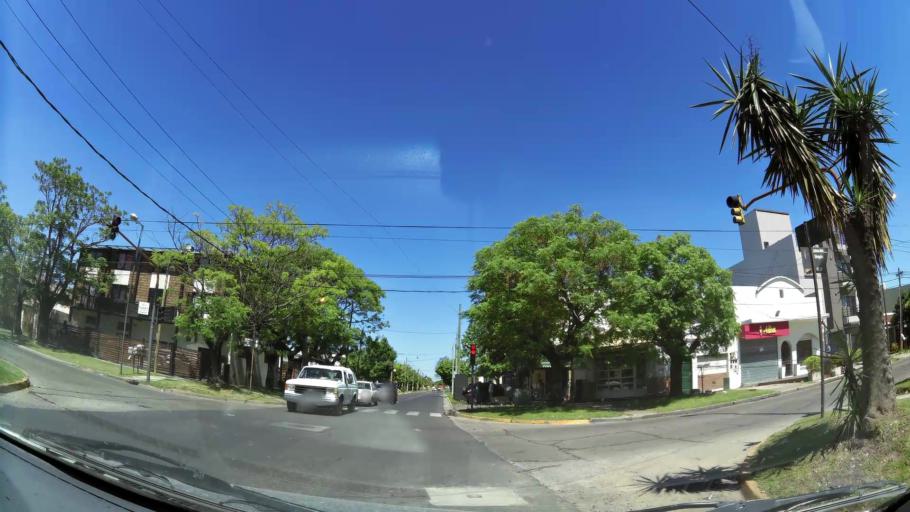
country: AR
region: Buenos Aires
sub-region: Partido de Quilmes
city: Quilmes
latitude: -34.7221
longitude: -58.2770
